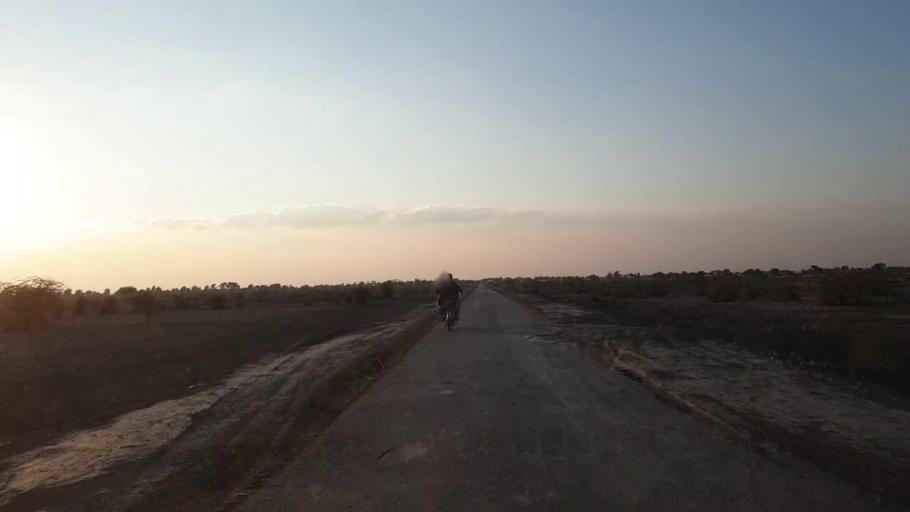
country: PK
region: Sindh
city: Shahpur Chakar
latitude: 26.1567
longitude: 68.5521
